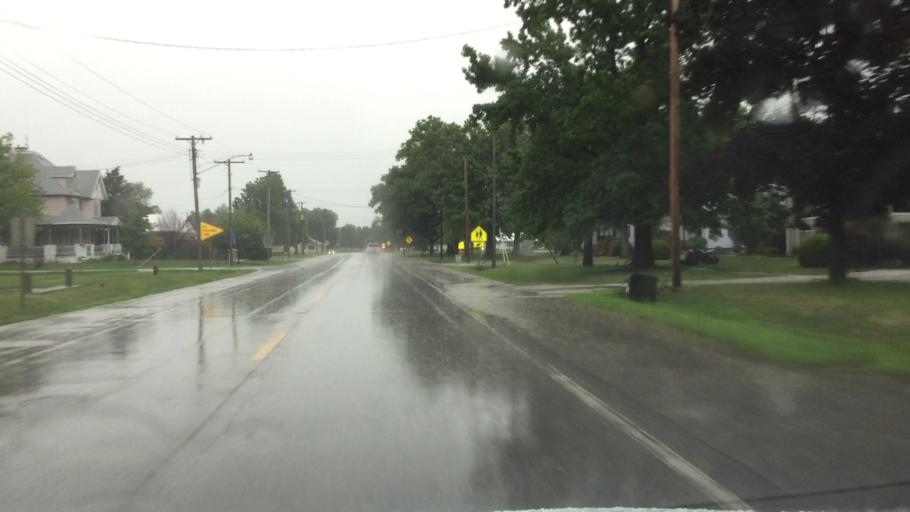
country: US
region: Illinois
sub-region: Hancock County
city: Carthage
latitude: 40.4200
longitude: -91.1362
